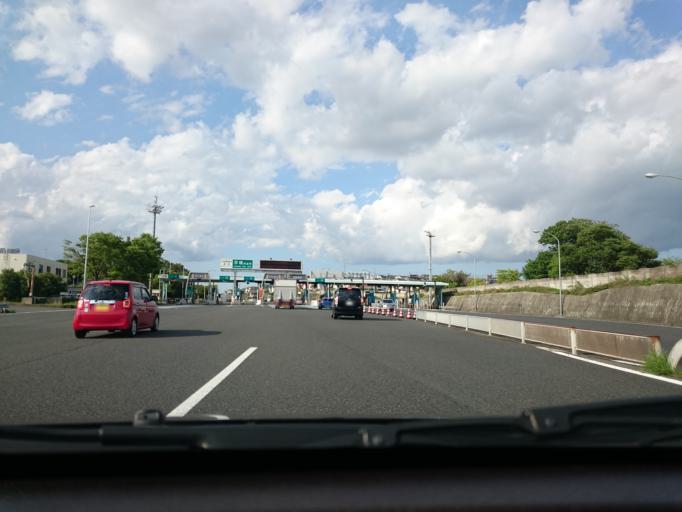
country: JP
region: Kanagawa
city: Oiso
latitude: 35.3361
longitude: 139.2949
